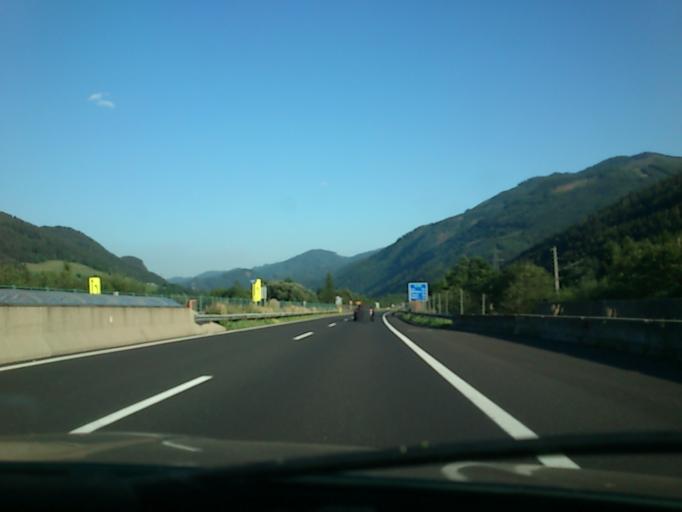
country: AT
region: Styria
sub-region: Politischer Bezirk Leoben
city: Kalwang
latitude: 47.4203
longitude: 14.7601
